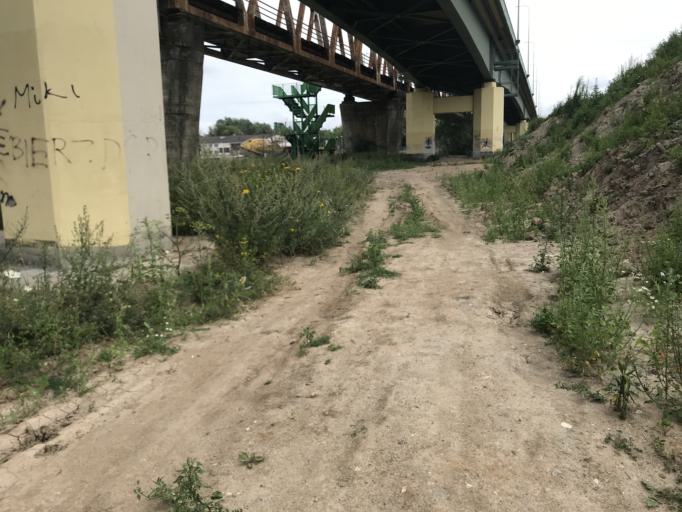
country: PL
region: Warmian-Masurian Voivodeship
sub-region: Powiat elblaski
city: Elblag
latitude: 54.1726
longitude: 19.3871
